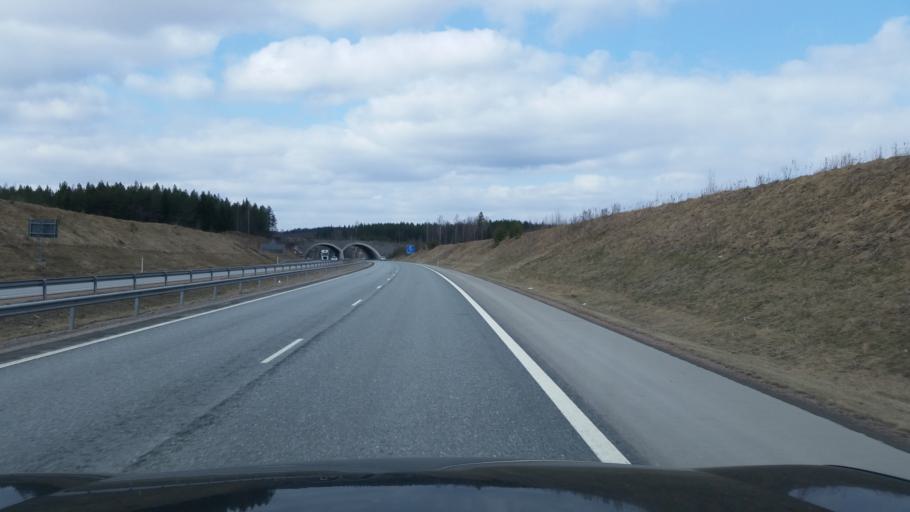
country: FI
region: Uusimaa
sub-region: Helsinki
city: Sammatti
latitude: 60.3755
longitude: 23.8259
